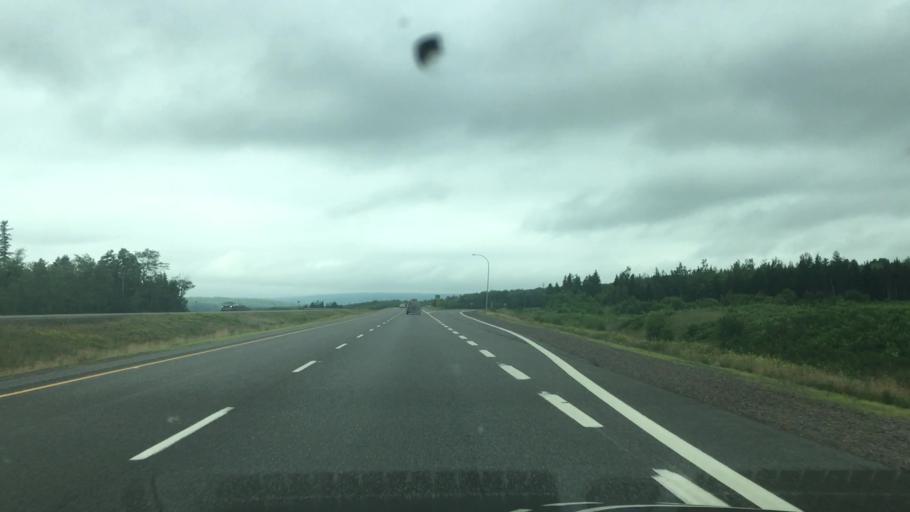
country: CA
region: Nova Scotia
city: Truro
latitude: 45.4348
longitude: -63.5805
